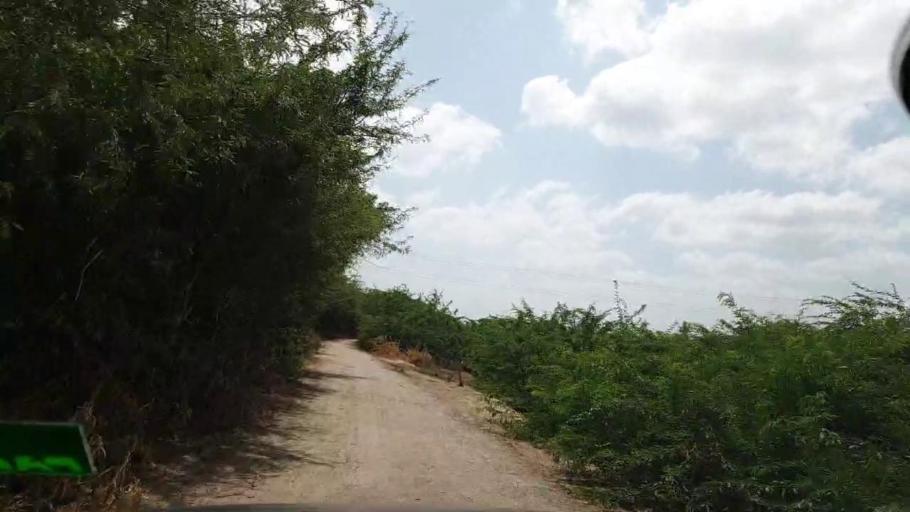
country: PK
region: Sindh
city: Kadhan
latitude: 24.5410
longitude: 69.2068
